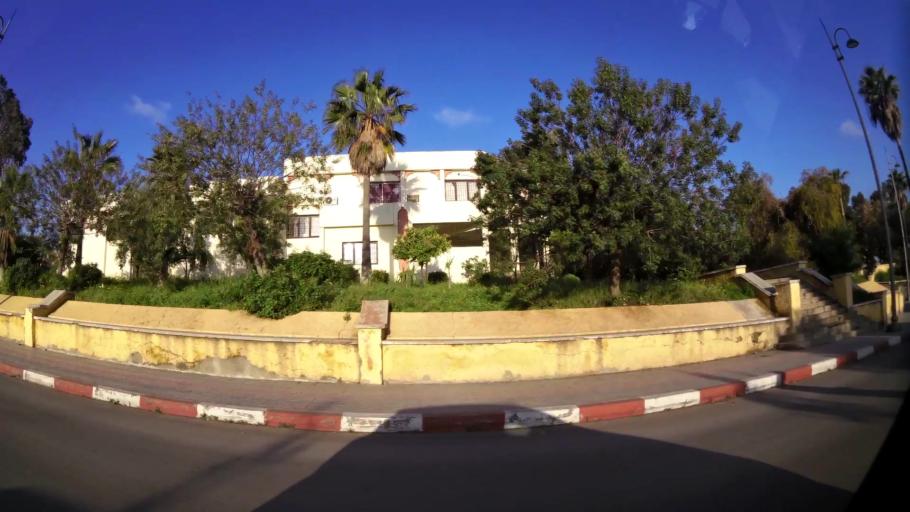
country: MA
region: Chaouia-Ouardigha
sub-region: Settat Province
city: Settat
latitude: 33.0064
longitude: -7.6166
